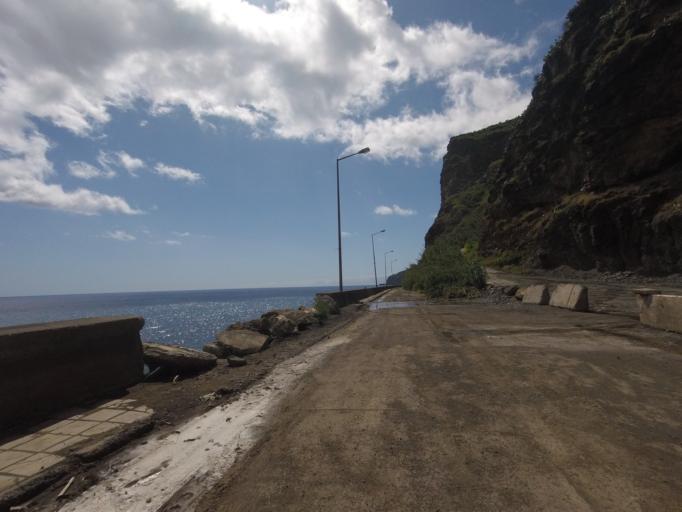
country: PT
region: Madeira
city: Ribeira Brava
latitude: 32.6759
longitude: -17.0736
